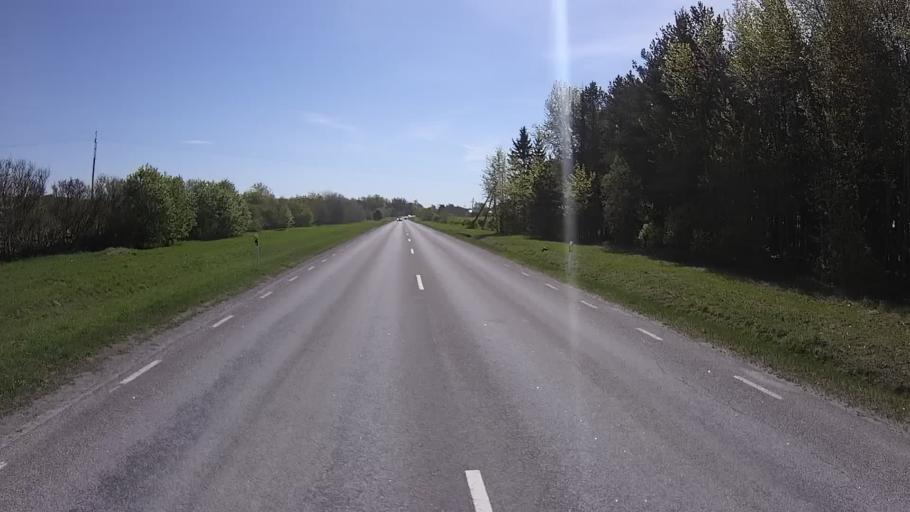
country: EE
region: Laeaene
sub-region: Ridala Parish
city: Uuemoisa
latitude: 58.8735
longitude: 23.6143
